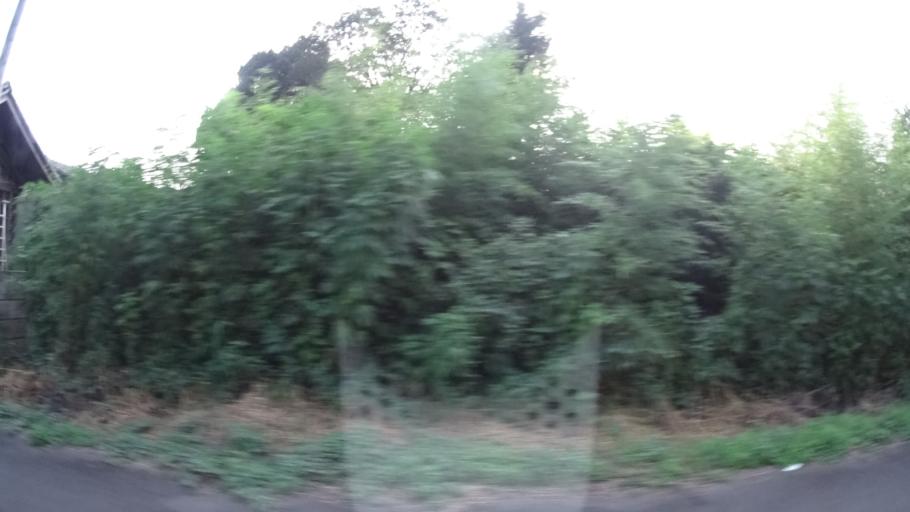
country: JP
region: Tochigi
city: Motegi
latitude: 36.5618
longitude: 140.1032
